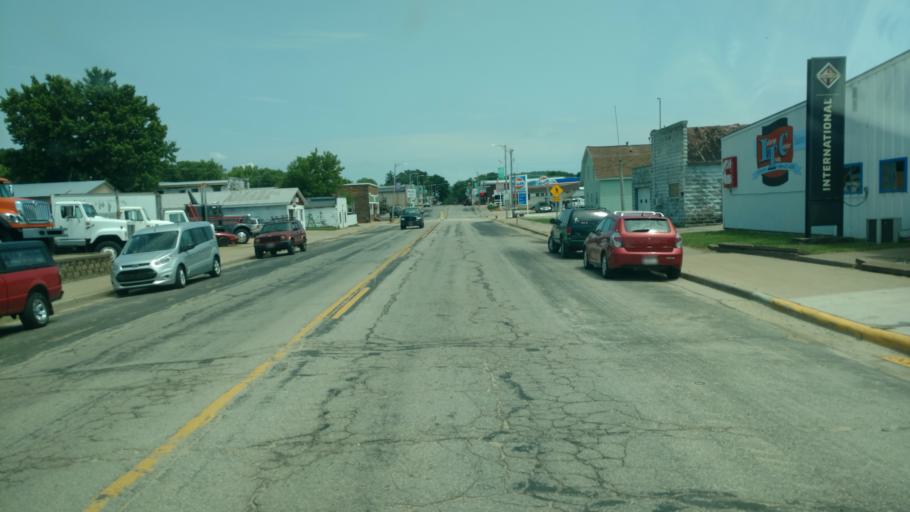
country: US
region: Wisconsin
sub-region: Monroe County
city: Cashton
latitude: 43.5743
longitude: -90.6401
